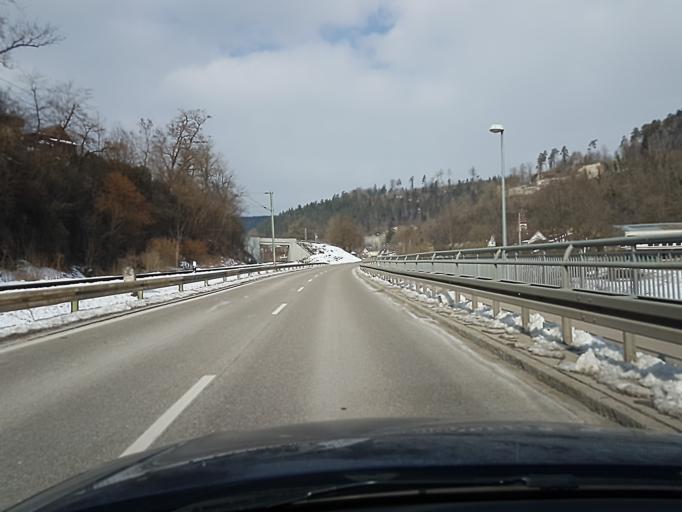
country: DE
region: Baden-Wuerttemberg
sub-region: Freiburg Region
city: Muhlheim am Bach
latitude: 48.3880
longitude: 8.6754
